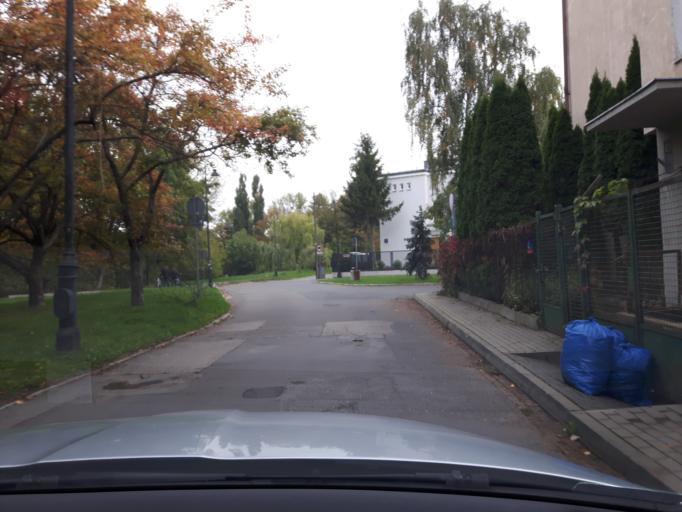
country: PL
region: Masovian Voivodeship
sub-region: Warszawa
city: Mokotow
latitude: 52.1861
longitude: 21.0283
